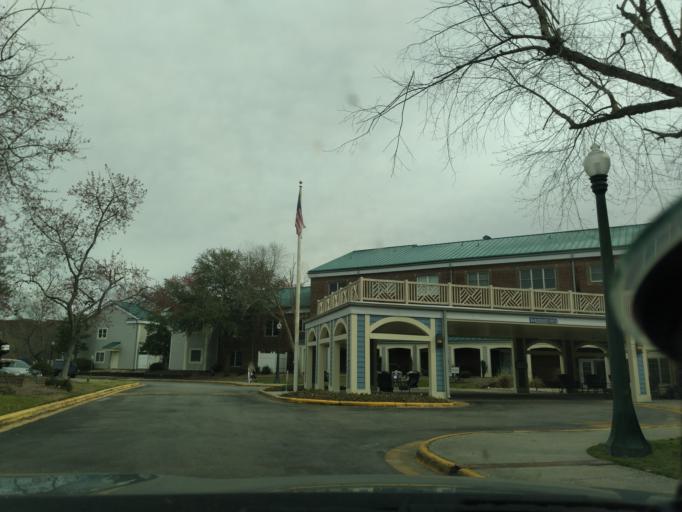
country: US
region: North Carolina
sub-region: Edgecombe County
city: Tarboro
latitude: 35.8953
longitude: -77.5349
